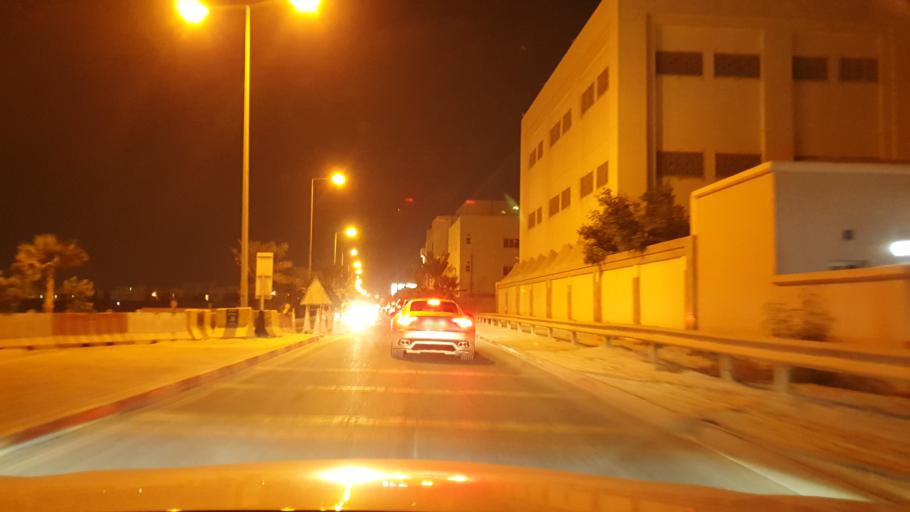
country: BH
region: Manama
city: Jidd Hafs
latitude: 26.1989
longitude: 50.5085
